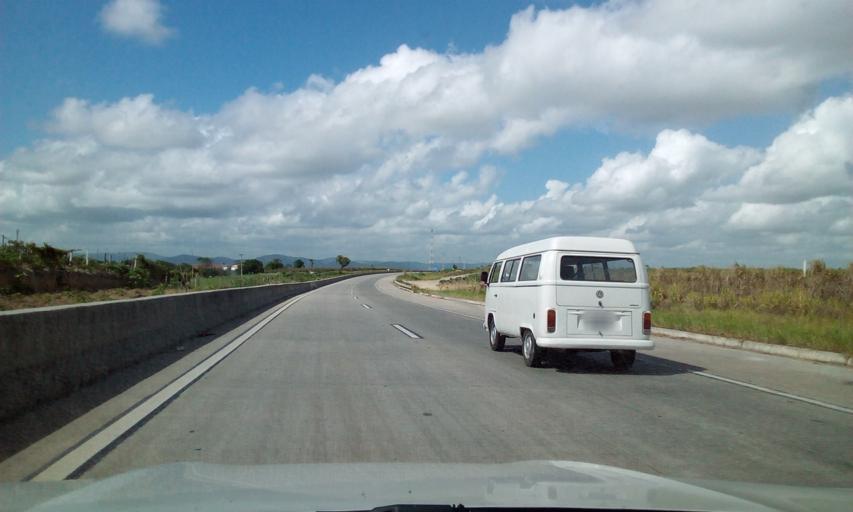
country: BR
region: Alagoas
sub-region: Messias
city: Messias
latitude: -9.3953
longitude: -35.8363
